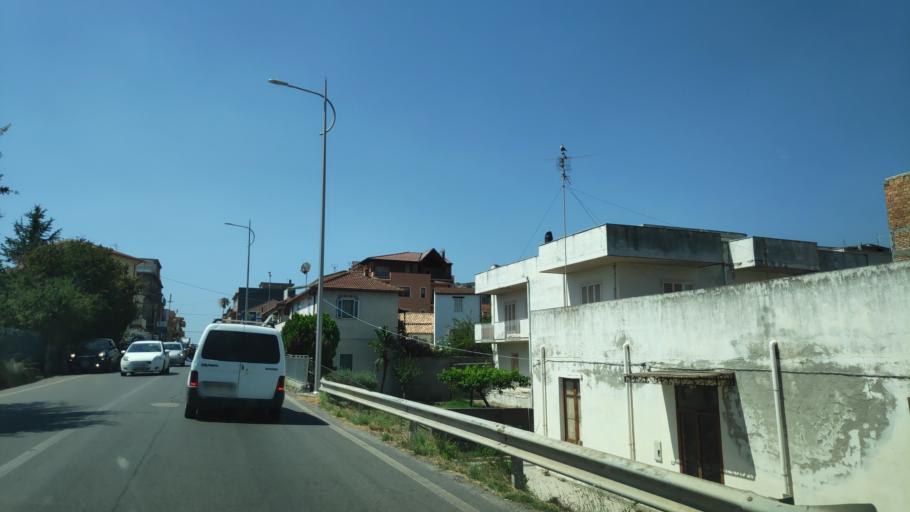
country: IT
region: Calabria
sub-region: Provincia di Reggio Calabria
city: Brancaleone-Marina
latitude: 37.9687
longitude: 16.1050
